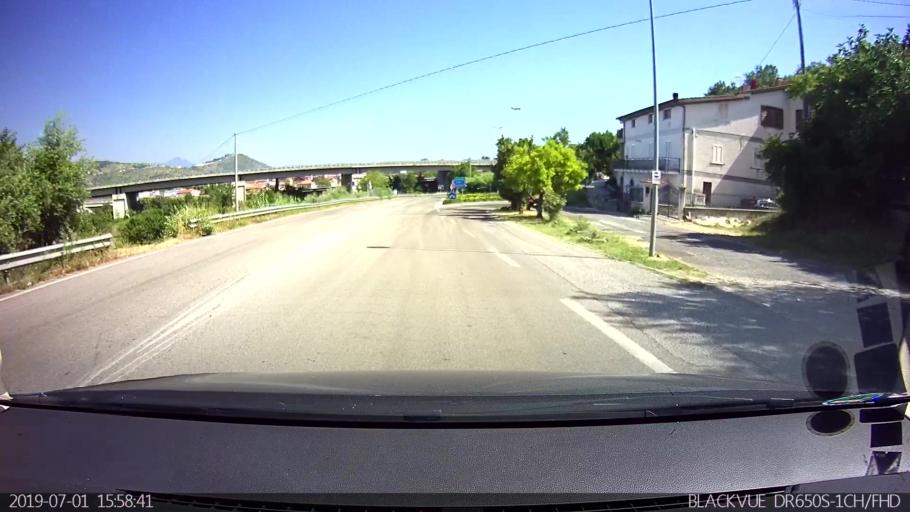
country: IT
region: Latium
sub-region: Provincia di Frosinone
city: Sant'Angelo in Villa-Giglio
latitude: 41.6659
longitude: 13.4241
